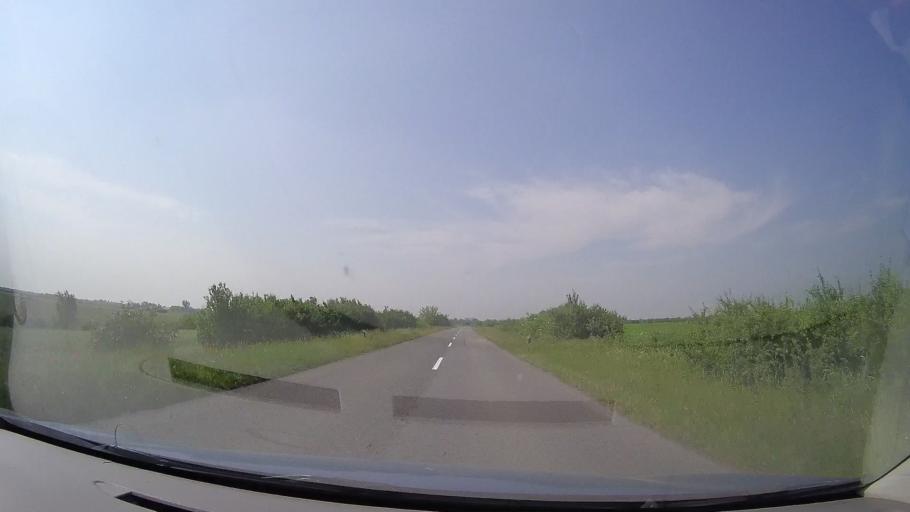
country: RS
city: Jarkovac
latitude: 45.2844
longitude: 20.7634
